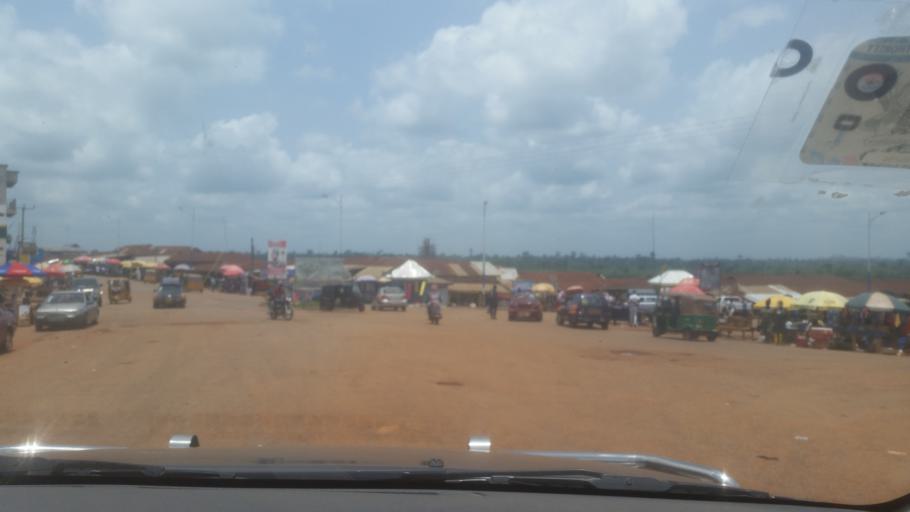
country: GH
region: Western
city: Bibiani
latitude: 6.8036
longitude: -2.5176
